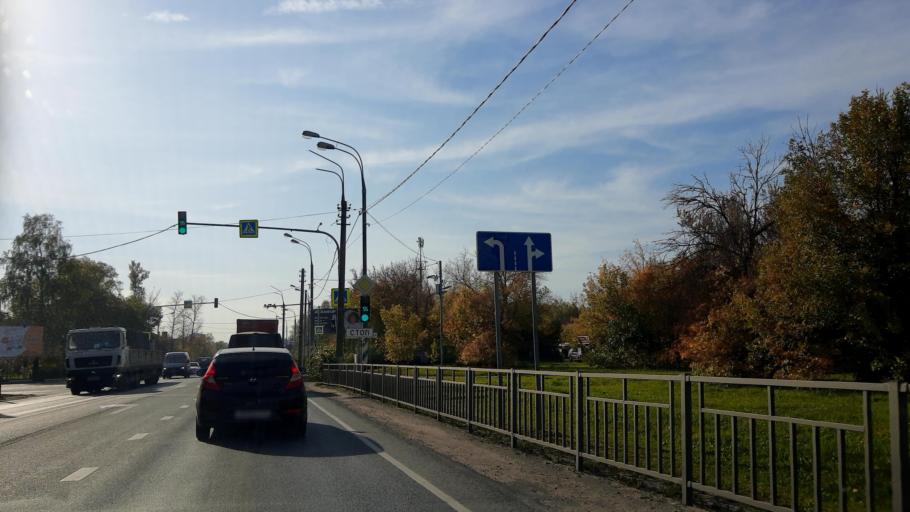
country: RU
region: Moskovskaya
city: Elektrostal'
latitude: 55.7905
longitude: 38.4306
